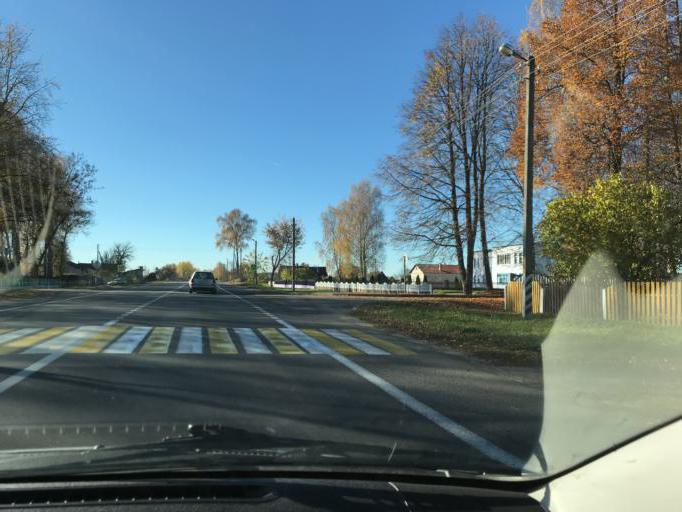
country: BY
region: Vitebsk
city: Lyepyel'
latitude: 54.9333
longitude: 28.7598
